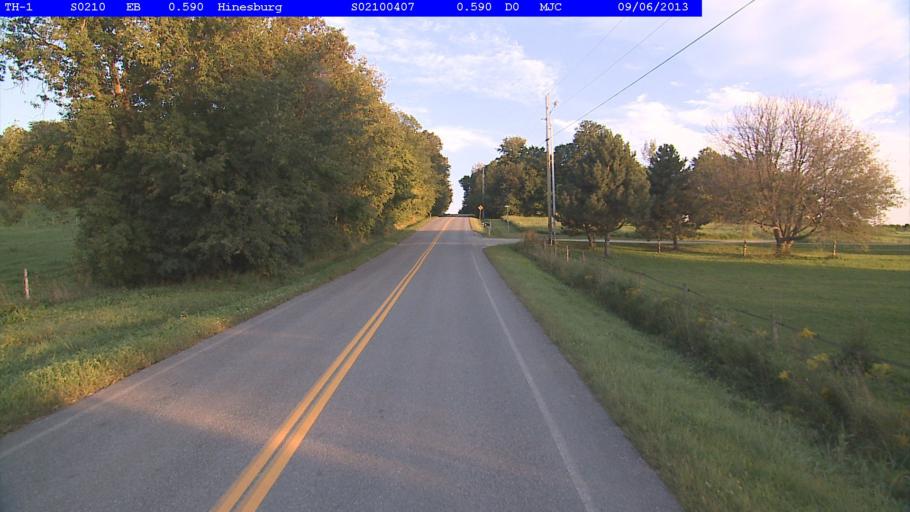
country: US
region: Vermont
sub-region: Chittenden County
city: Hinesburg
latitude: 44.3556
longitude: -73.1553
